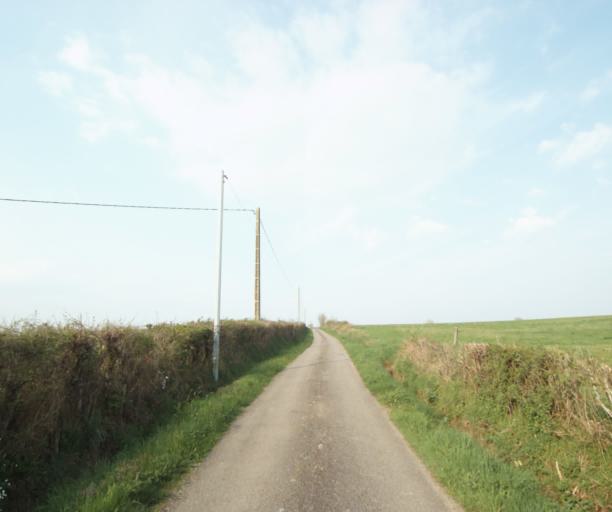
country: FR
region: Bourgogne
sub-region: Departement de Saone-et-Loire
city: Matour
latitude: 46.4636
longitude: 4.4492
